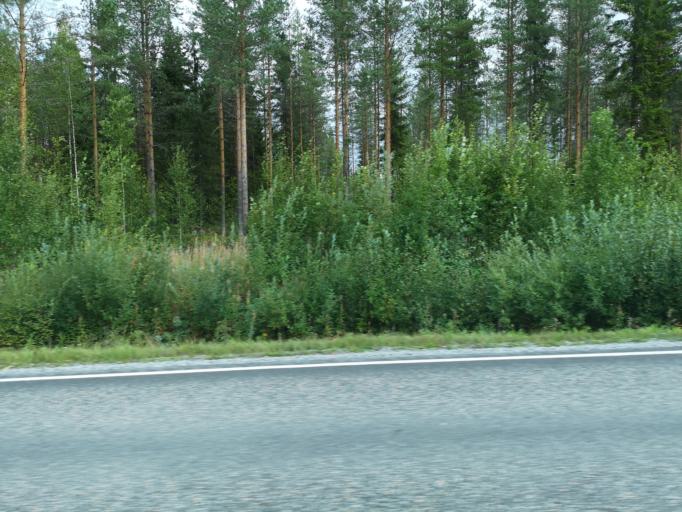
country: FI
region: Central Finland
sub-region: Jyvaeskylae
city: Hankasalmi
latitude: 62.3548
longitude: 26.4551
